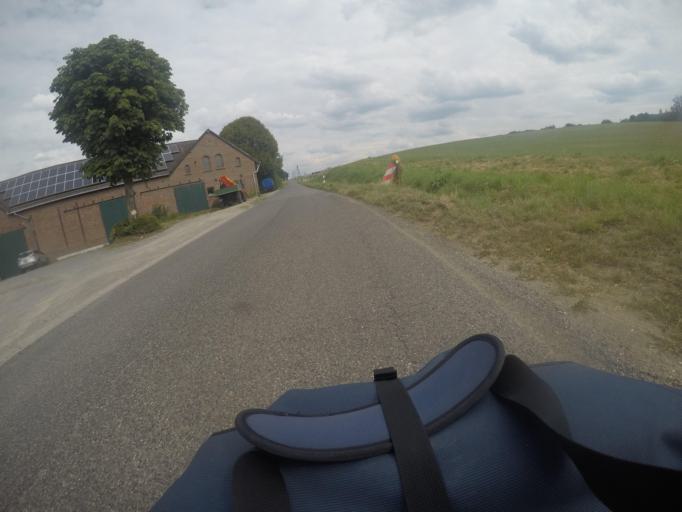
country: DE
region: North Rhine-Westphalia
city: Haan
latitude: 51.2177
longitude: 7.0281
